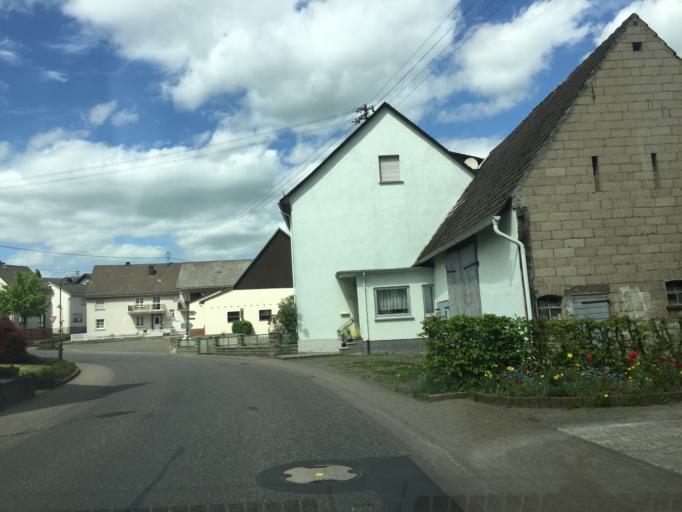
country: DE
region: Rheinland-Pfalz
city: Meudt
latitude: 50.4917
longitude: 7.8982
